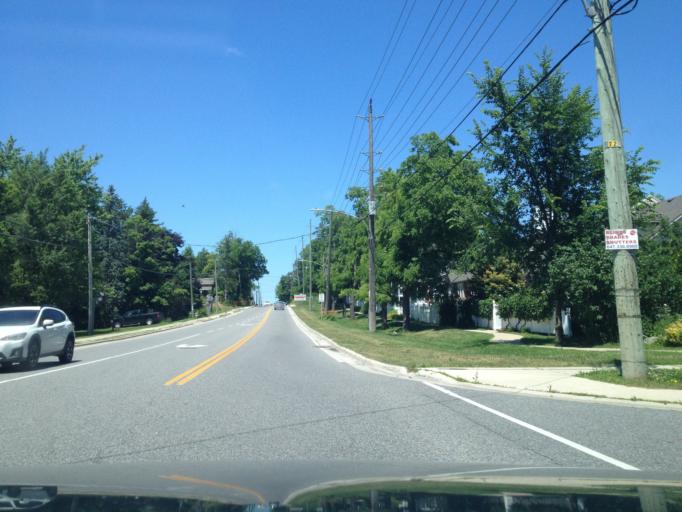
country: CA
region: Ontario
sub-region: Wellington County
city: Guelph
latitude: 43.6108
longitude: -80.1327
